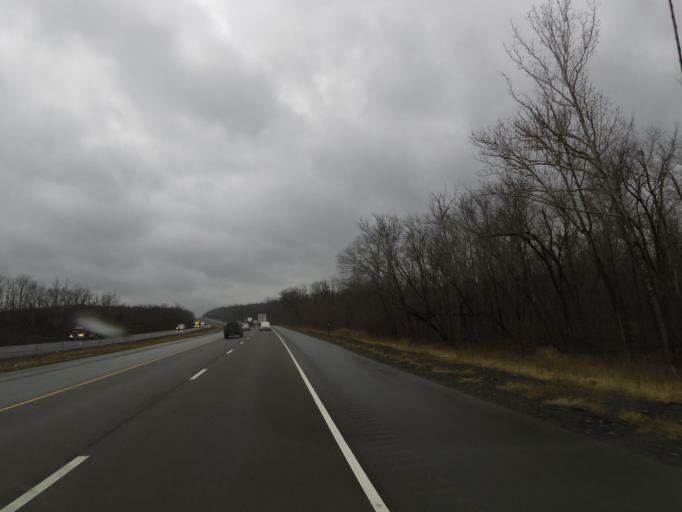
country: US
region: Illinois
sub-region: Williamson County
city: Marion
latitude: 37.7000
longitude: -88.9653
